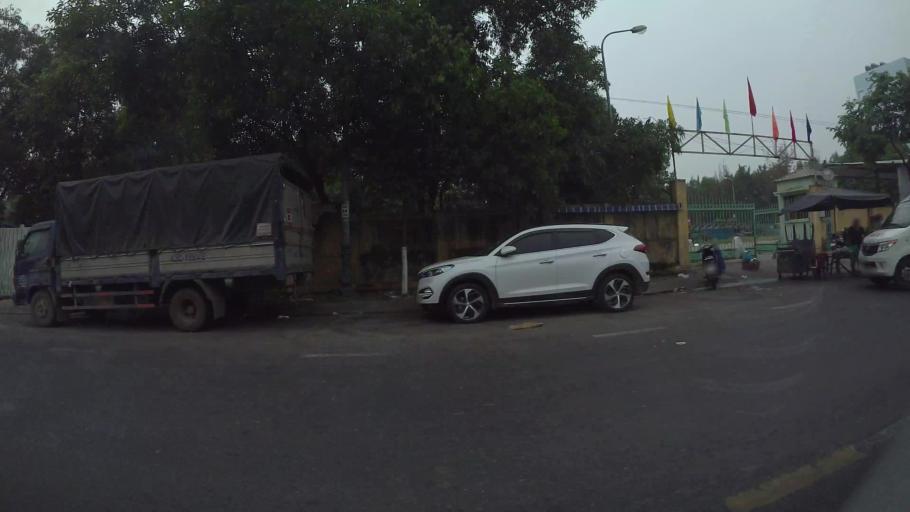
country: VN
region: Da Nang
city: Cam Le
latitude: 16.0307
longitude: 108.2189
